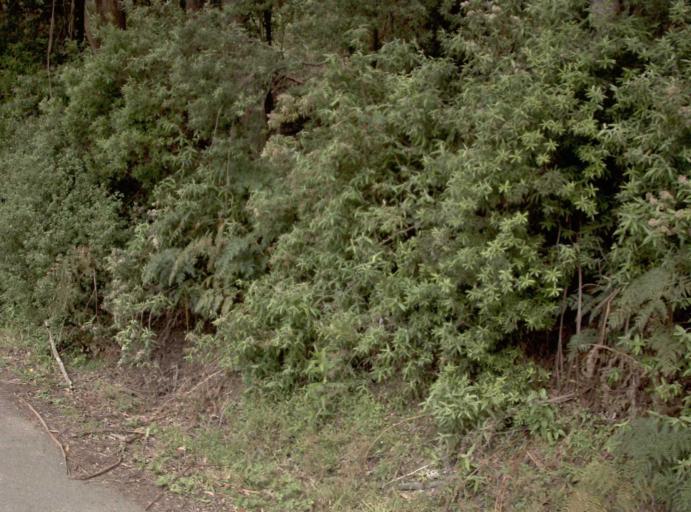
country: AU
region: Victoria
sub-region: Latrobe
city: Traralgon
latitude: -38.4264
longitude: 146.5669
